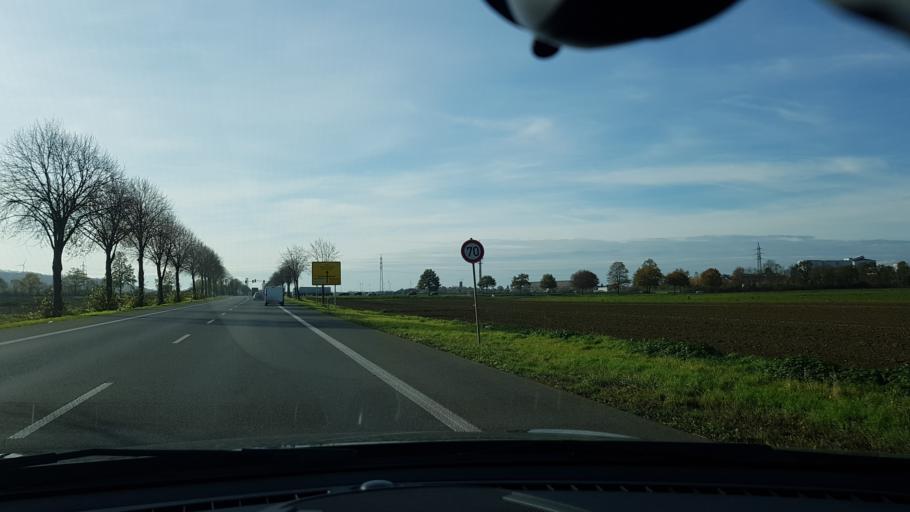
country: DE
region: North Rhine-Westphalia
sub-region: Regierungsbezirk Dusseldorf
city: Grevenbroich
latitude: 51.0955
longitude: 6.6184
